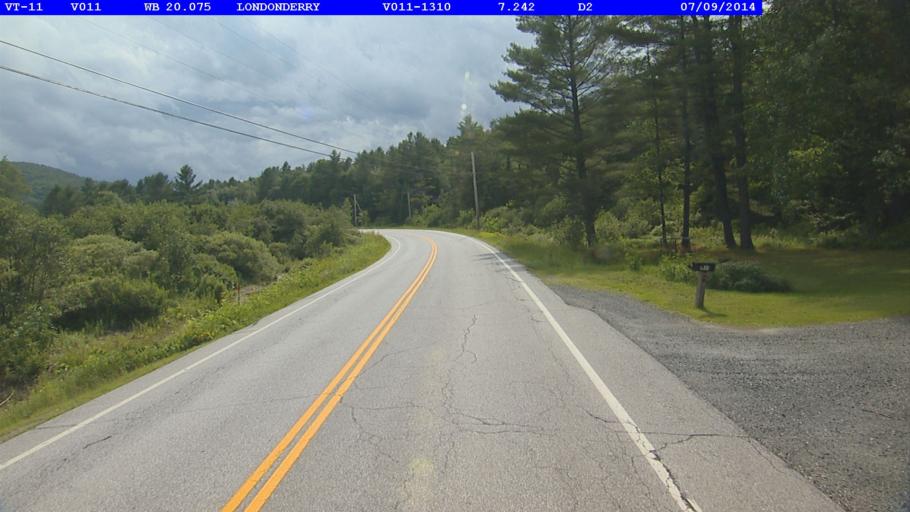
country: US
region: Vermont
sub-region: Windsor County
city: Chester
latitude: 43.2242
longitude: -72.7326
